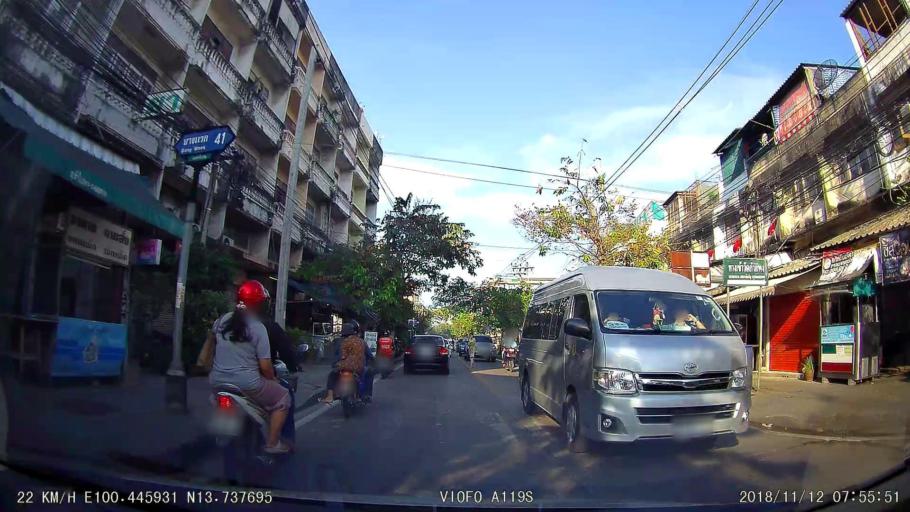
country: TH
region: Bangkok
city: Phasi Charoen
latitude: 13.7376
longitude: 100.4461
